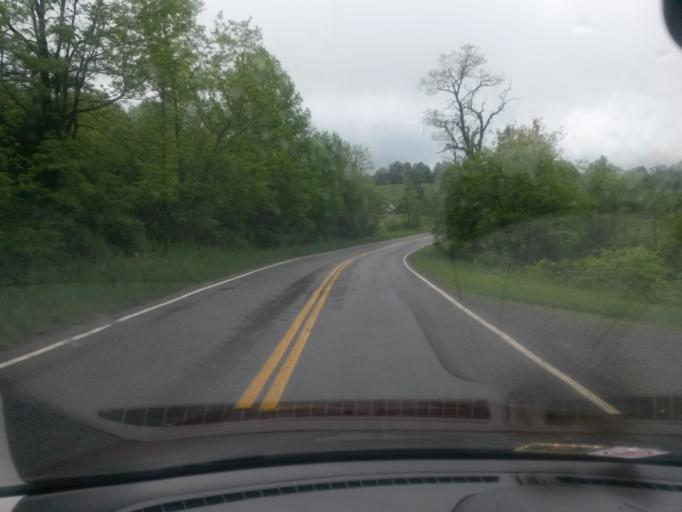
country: US
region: Virginia
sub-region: Patrick County
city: Stuart
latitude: 36.7471
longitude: -80.3908
